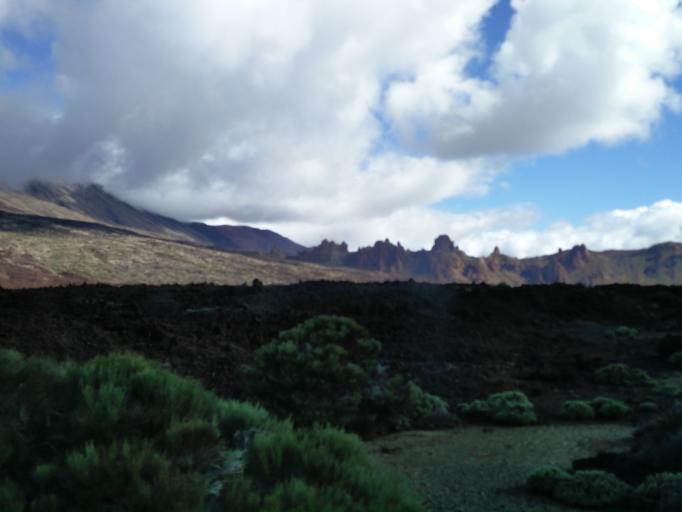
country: ES
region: Canary Islands
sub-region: Provincia de Santa Cruz de Tenerife
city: Vilaflor
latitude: 28.2110
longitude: -16.6575
